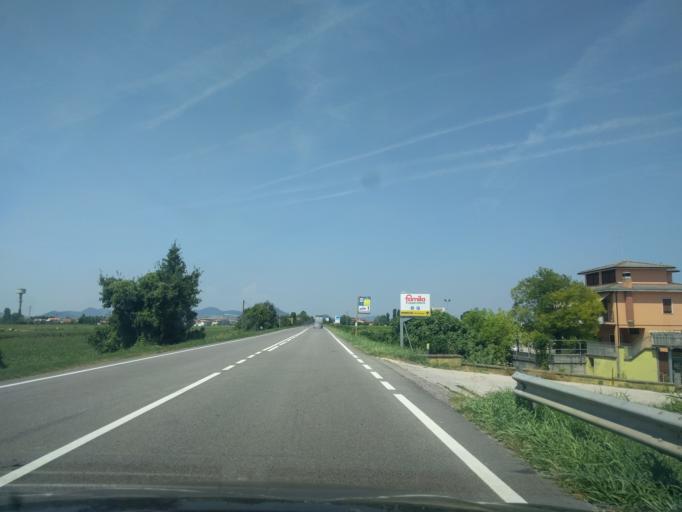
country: IT
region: Veneto
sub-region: Provincia di Padova
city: Solesino
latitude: 45.1633
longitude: 11.7565
